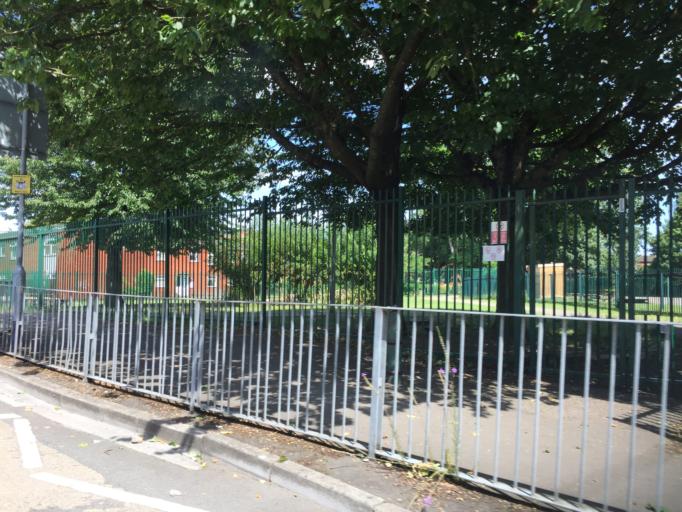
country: GB
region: Wales
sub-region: Newport
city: Newport
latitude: 51.5772
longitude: -2.9934
